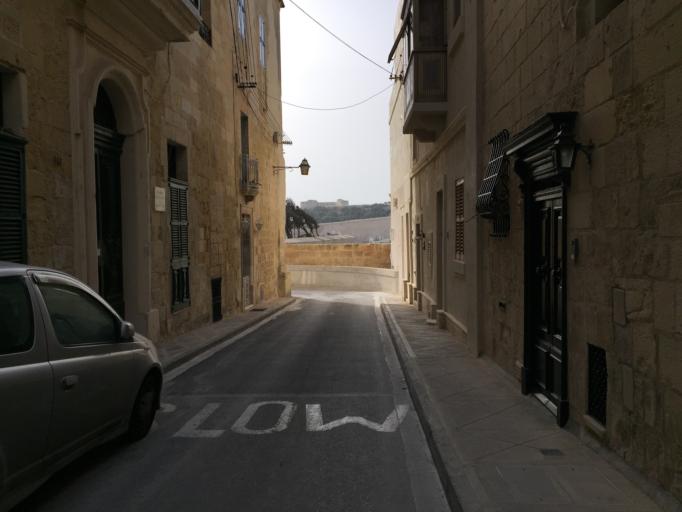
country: MT
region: L-Isla
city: Senglea
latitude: 35.8902
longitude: 14.5149
